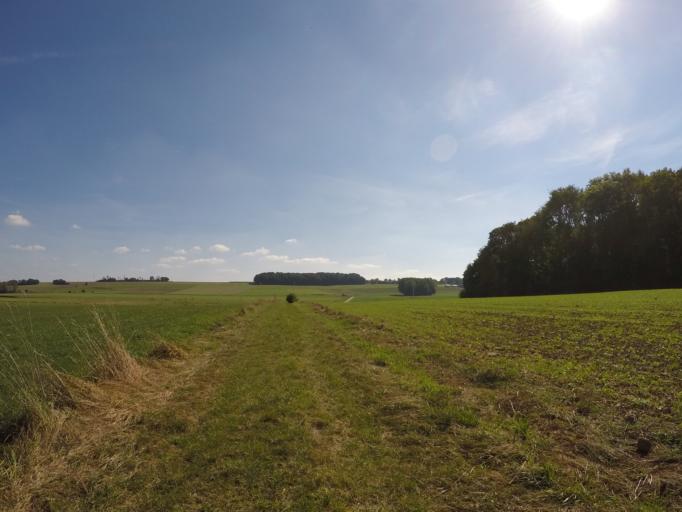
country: BE
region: Wallonia
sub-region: Province de Namur
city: Assesse
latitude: 50.3106
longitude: 5.0315
